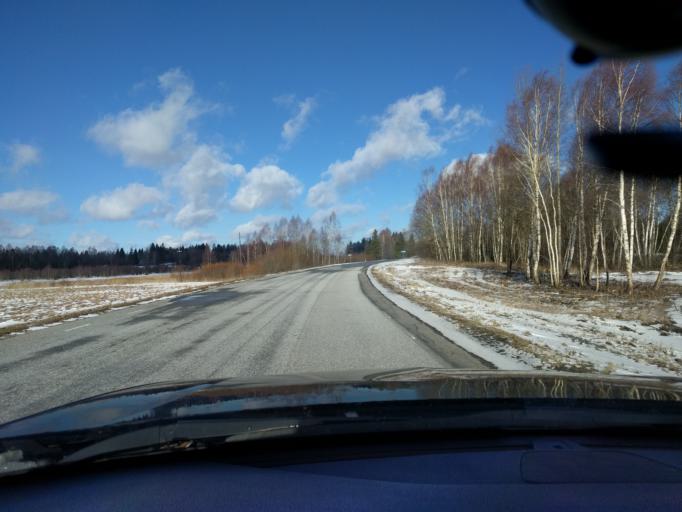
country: EE
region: Harju
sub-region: Raasiku vald
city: Raasiku
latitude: 59.3142
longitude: 25.1607
